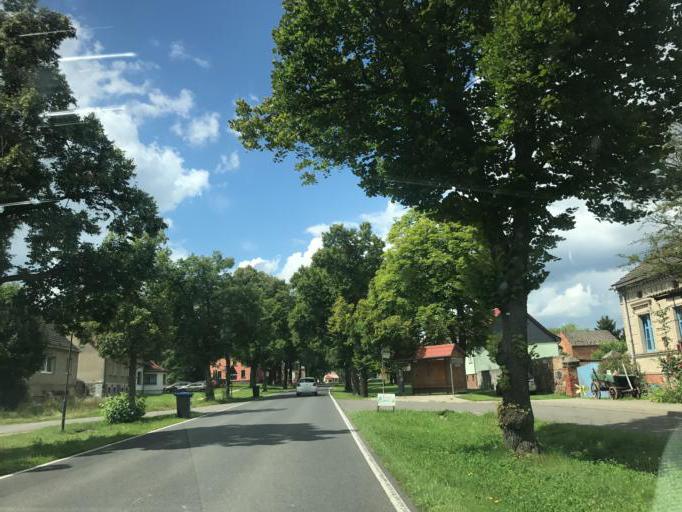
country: DE
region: Brandenburg
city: Grosswoltersdorf
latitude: 53.0708
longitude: 13.0933
